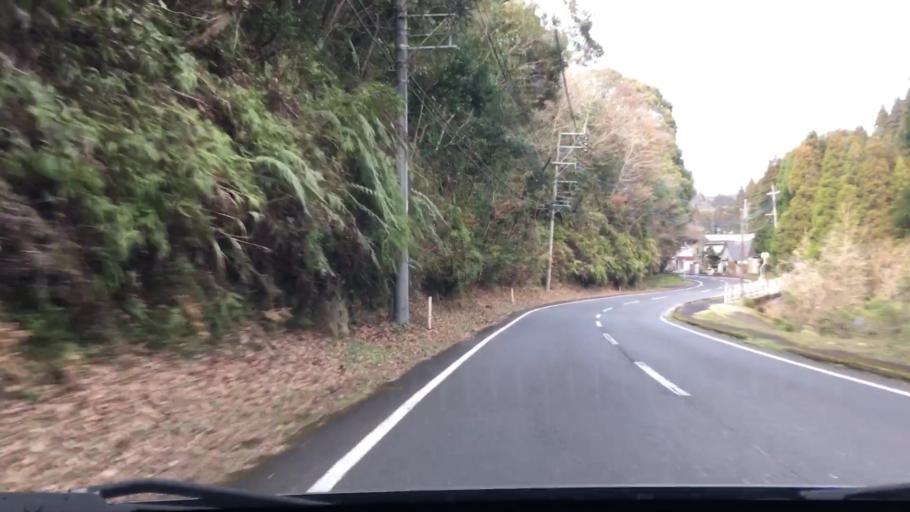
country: JP
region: Miyazaki
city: Kushima
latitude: 31.5432
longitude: 131.2418
